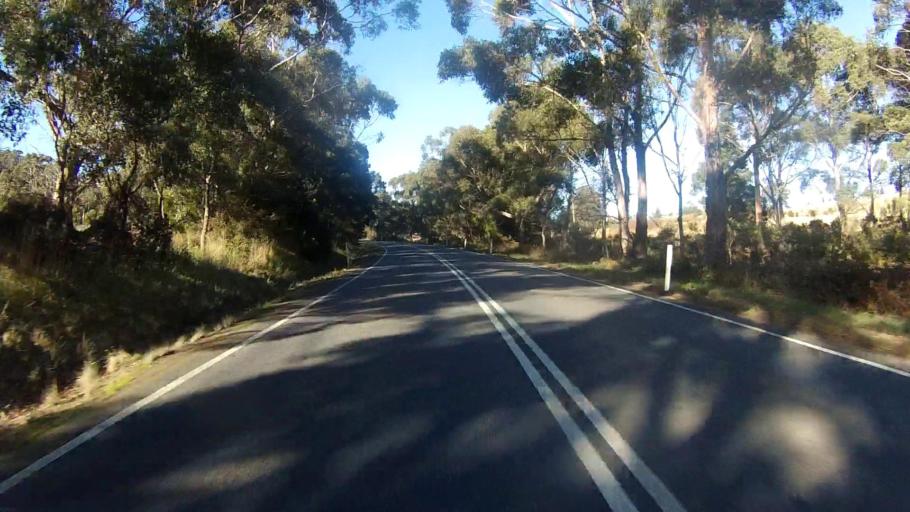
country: AU
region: Tasmania
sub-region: Sorell
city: Sorell
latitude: -42.8221
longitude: 147.8036
